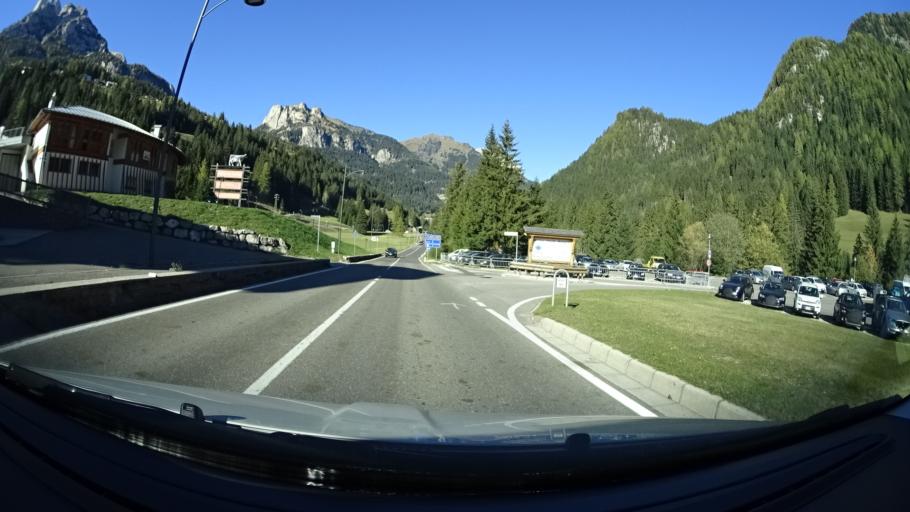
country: IT
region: Trentino-Alto Adige
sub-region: Provincia di Trento
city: Mazzin
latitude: 46.4433
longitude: 11.6959
